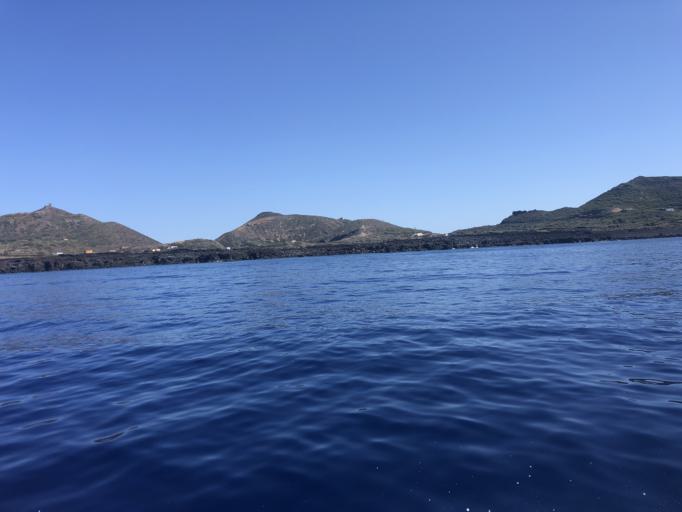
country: IT
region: Sicily
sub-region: Agrigento
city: Lampedusa
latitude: 35.8752
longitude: 12.8536
